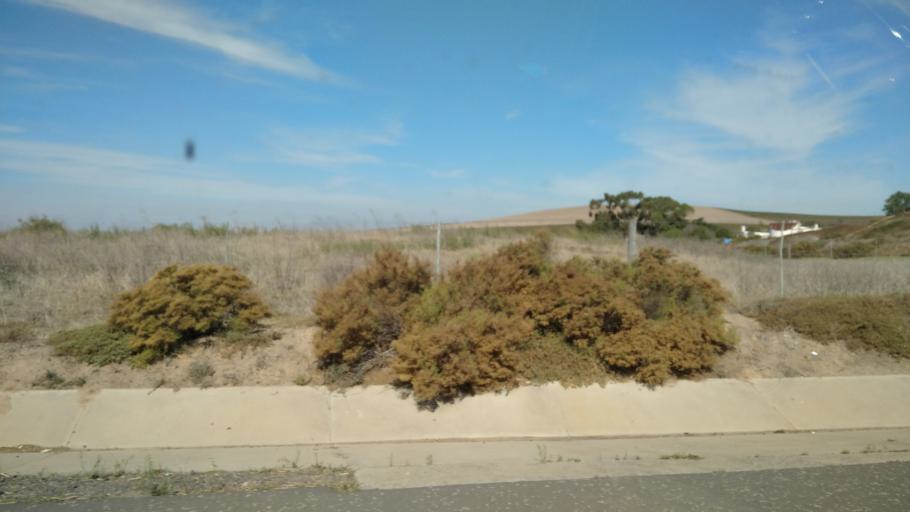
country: ZA
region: Western Cape
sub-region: City of Cape Town
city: Atlantis
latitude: -33.6633
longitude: 18.5612
